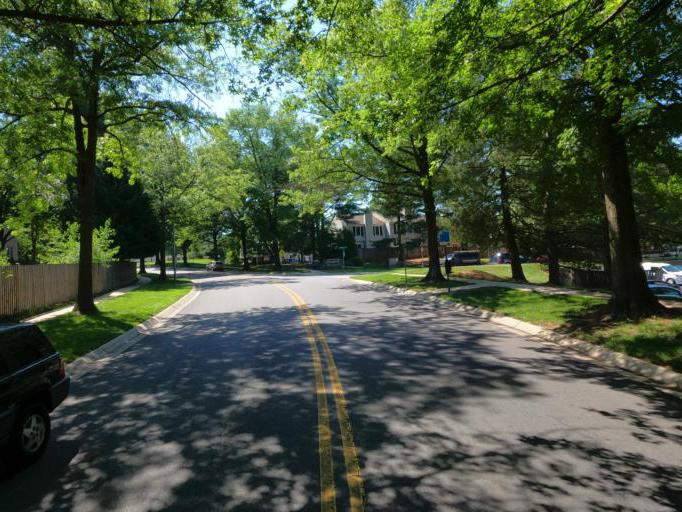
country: US
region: Maryland
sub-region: Montgomery County
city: Germantown
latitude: 39.1904
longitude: -77.2706
